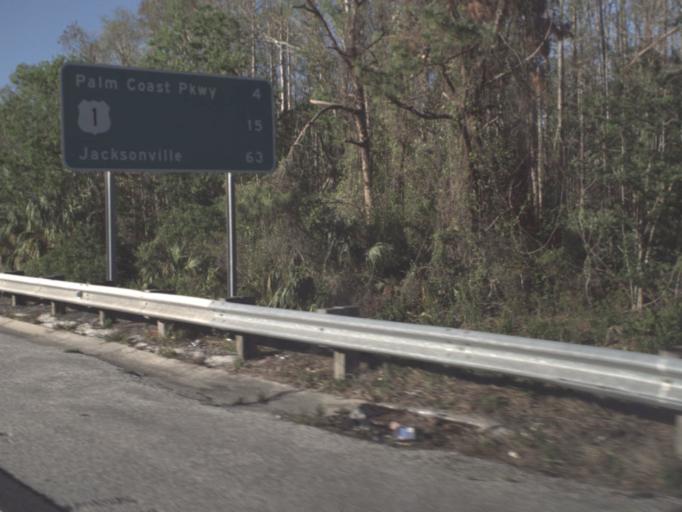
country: US
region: Florida
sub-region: Flagler County
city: Flagler Beach
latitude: 29.4940
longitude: -81.1905
